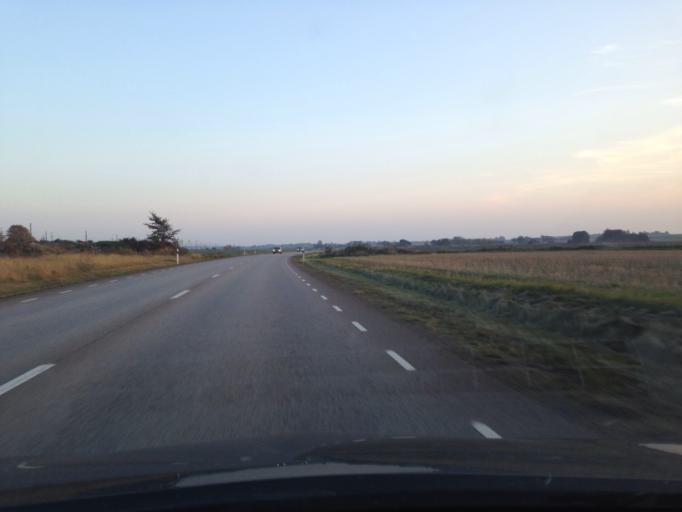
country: SE
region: Skane
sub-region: Bastads Kommun
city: Forslov
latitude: 56.3413
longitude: 12.8024
